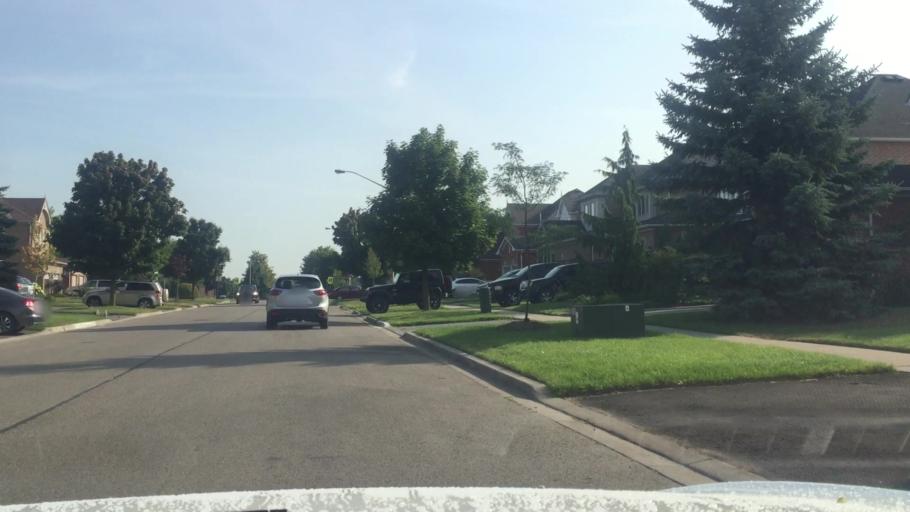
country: CA
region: Ontario
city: Oshawa
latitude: 43.9046
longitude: -78.7815
